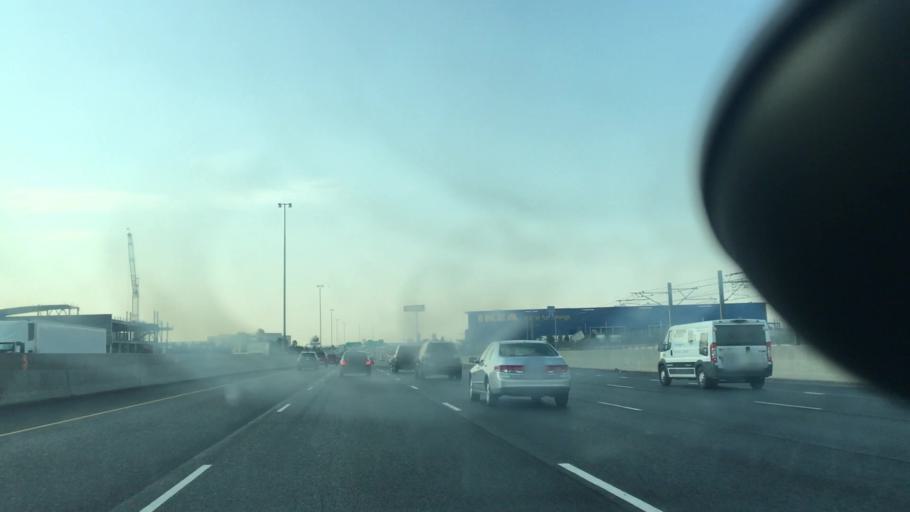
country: US
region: Colorado
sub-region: Arapahoe County
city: Centennial
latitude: 39.5754
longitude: -104.8761
